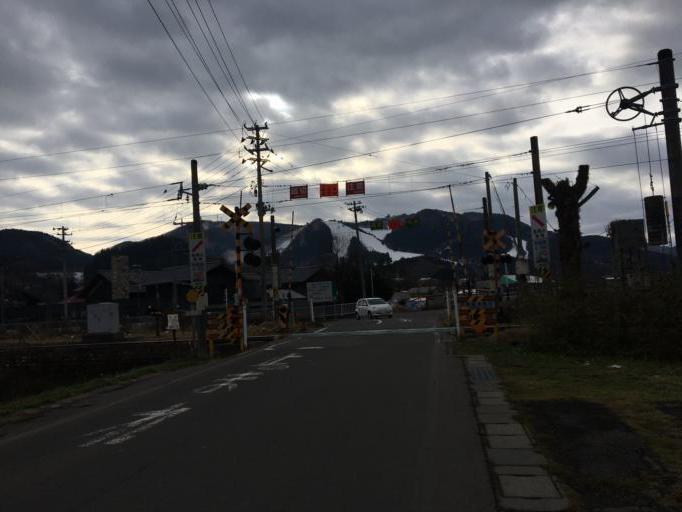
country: JP
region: Aomori
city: Hirosaki
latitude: 40.5214
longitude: 140.5639
